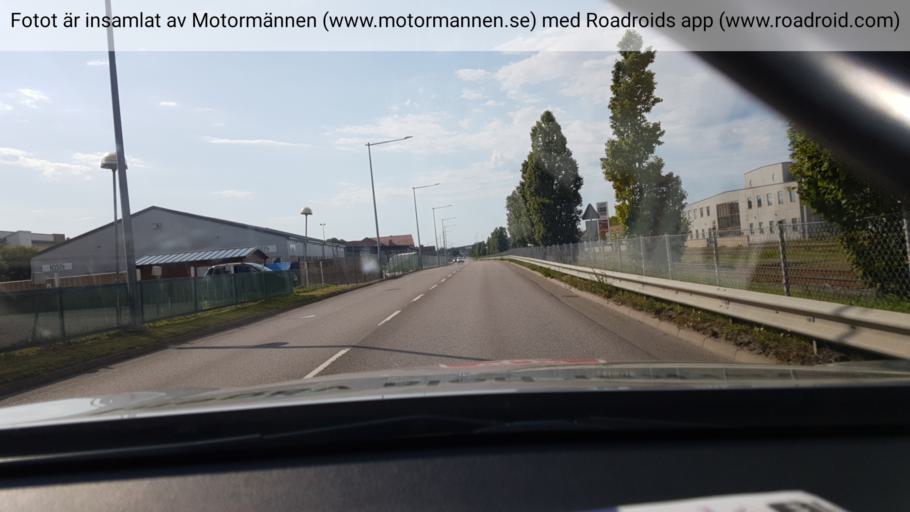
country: SE
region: Vaestra Goetaland
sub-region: Lidkopings Kommun
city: Lidkoping
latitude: 58.5016
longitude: 13.1754
